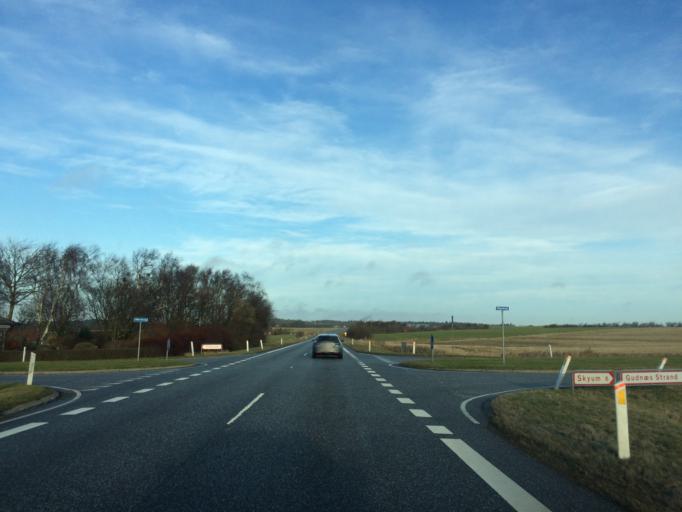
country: DK
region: North Denmark
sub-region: Thisted Kommune
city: Hurup
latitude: 56.8200
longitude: 8.4926
